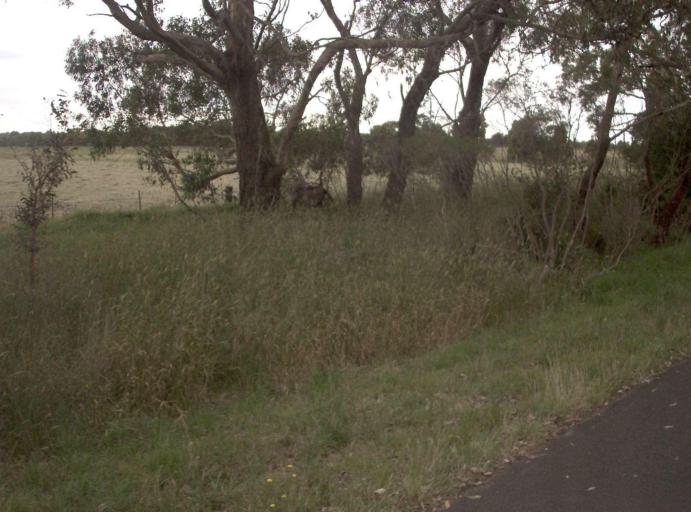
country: AU
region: Victoria
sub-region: Latrobe
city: Traralgon
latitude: -38.5520
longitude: 146.7417
